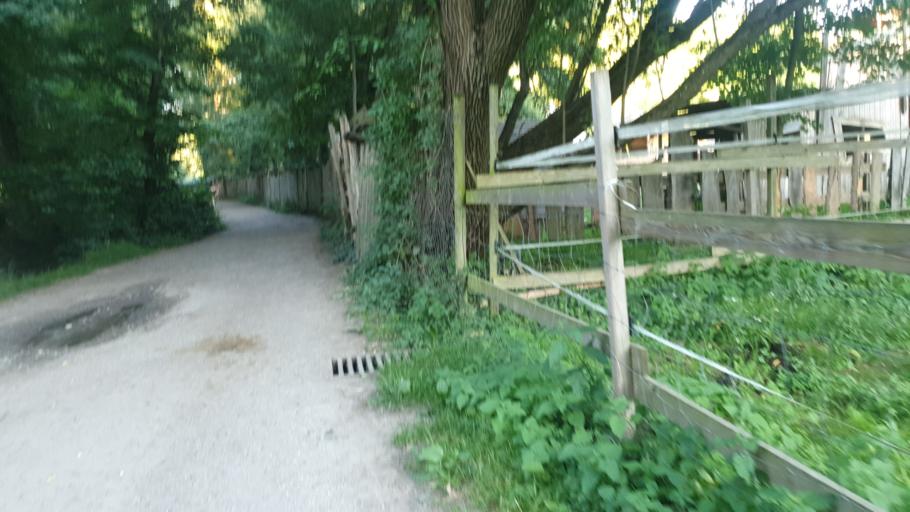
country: DE
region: Baden-Wuerttemberg
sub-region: Freiburg Region
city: Merzhausen
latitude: 47.9739
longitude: 7.8219
